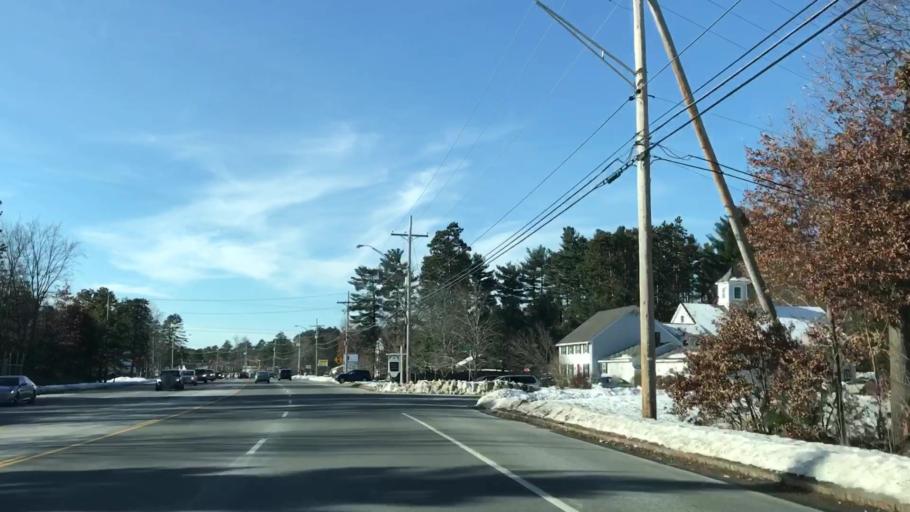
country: US
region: New Hampshire
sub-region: Hillsborough County
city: Hollis
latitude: 42.8109
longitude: -71.5766
